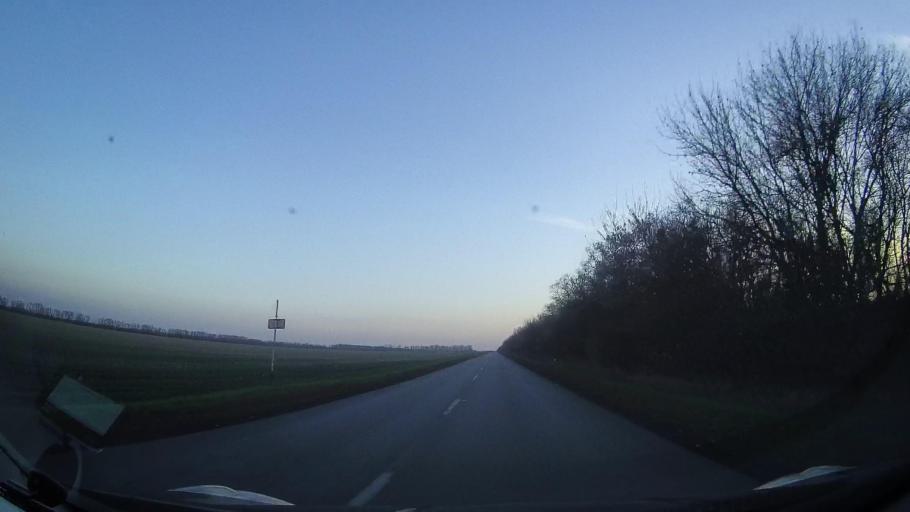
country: RU
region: Rostov
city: Zernograd
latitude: 47.0392
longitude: 40.3916
